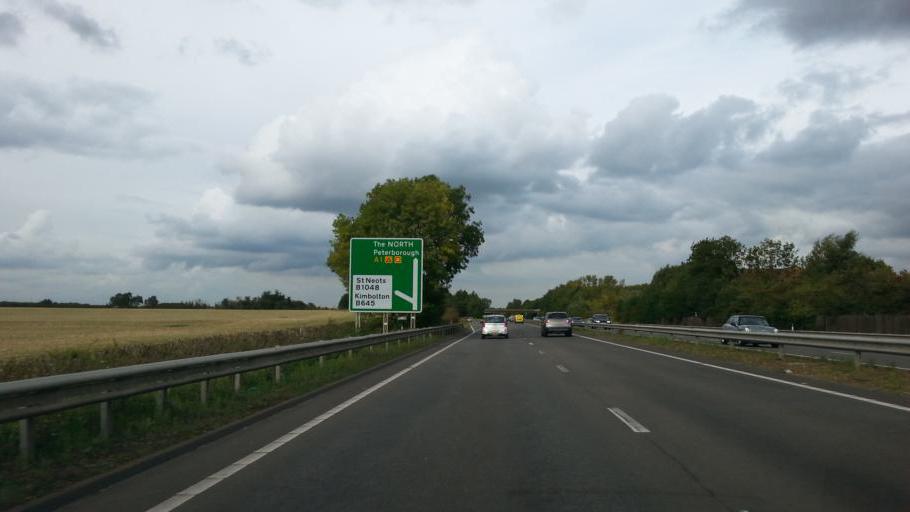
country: GB
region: England
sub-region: Cambridgeshire
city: Eaton Socon
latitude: 52.2332
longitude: -0.2882
